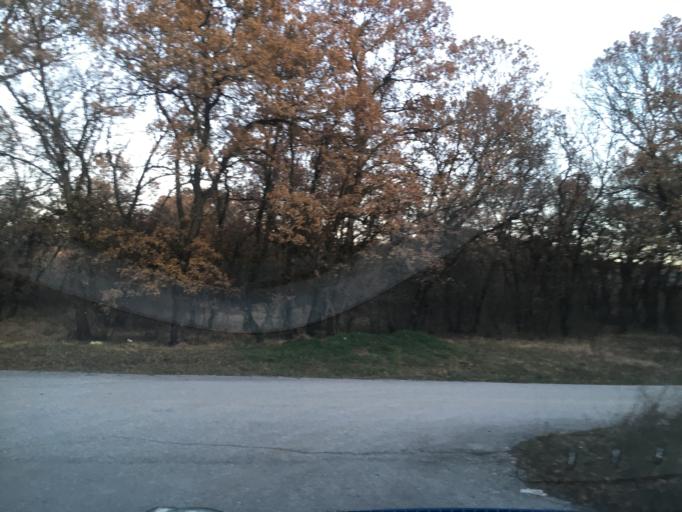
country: GR
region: West Macedonia
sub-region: Nomos Kozanis
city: Koila
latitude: 40.3306
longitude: 21.8318
